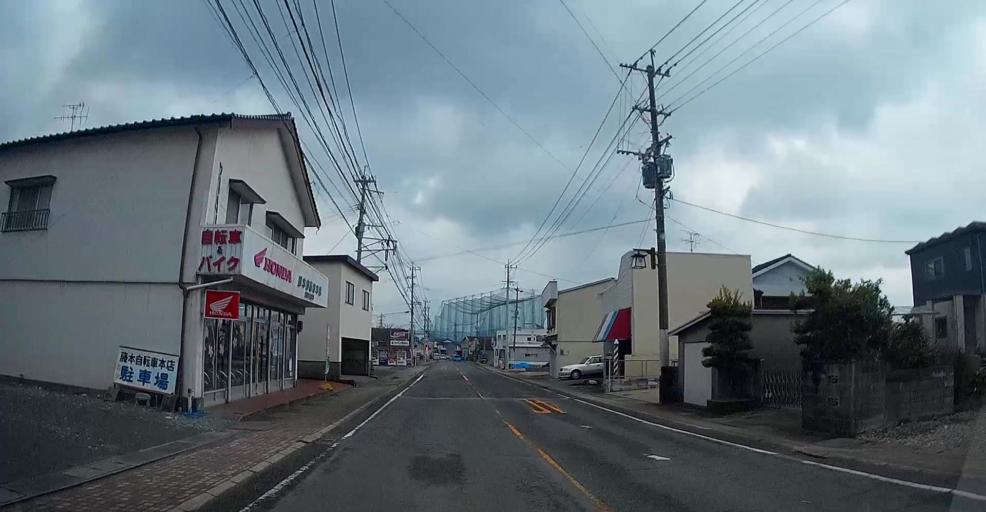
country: JP
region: Kumamoto
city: Matsubase
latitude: 32.6513
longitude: 130.6854
